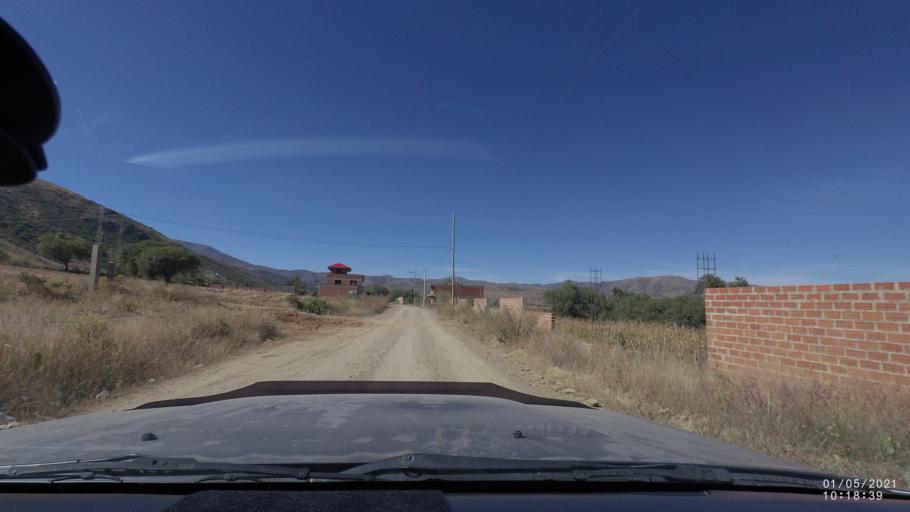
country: BO
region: Cochabamba
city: Capinota
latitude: -17.5555
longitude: -66.2082
